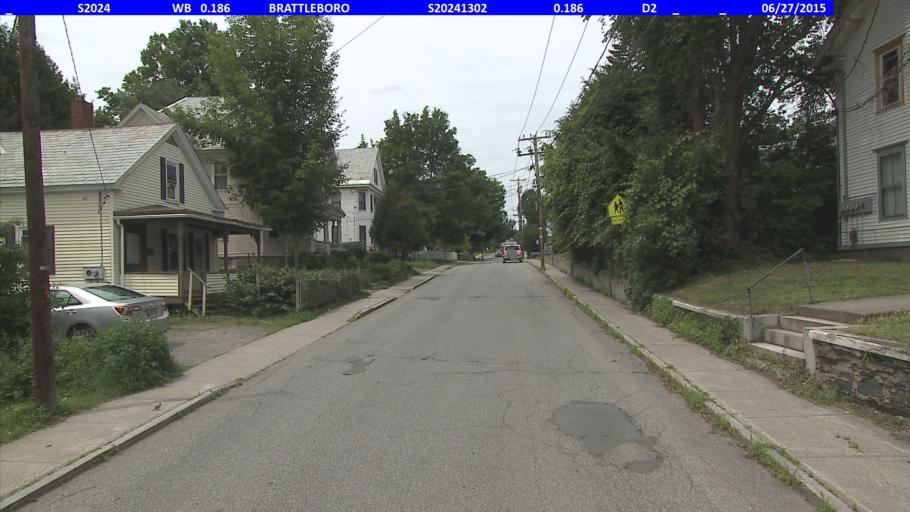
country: US
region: Vermont
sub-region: Windham County
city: Brattleboro
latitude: 42.8522
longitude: -72.5629
